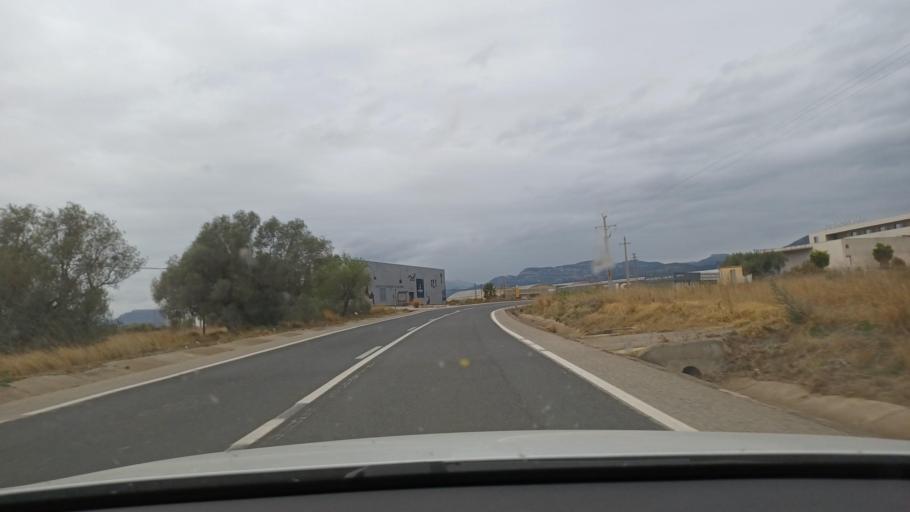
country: ES
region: Valencia
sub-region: Provincia de Castello
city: Rosell
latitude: 40.6303
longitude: 0.2983
